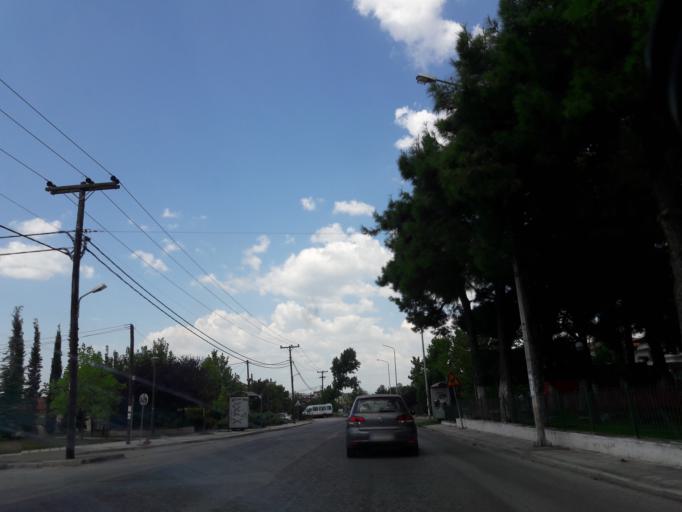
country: GR
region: Central Macedonia
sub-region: Nomos Thessalonikis
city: Thermi
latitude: 40.5256
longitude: 23.0486
